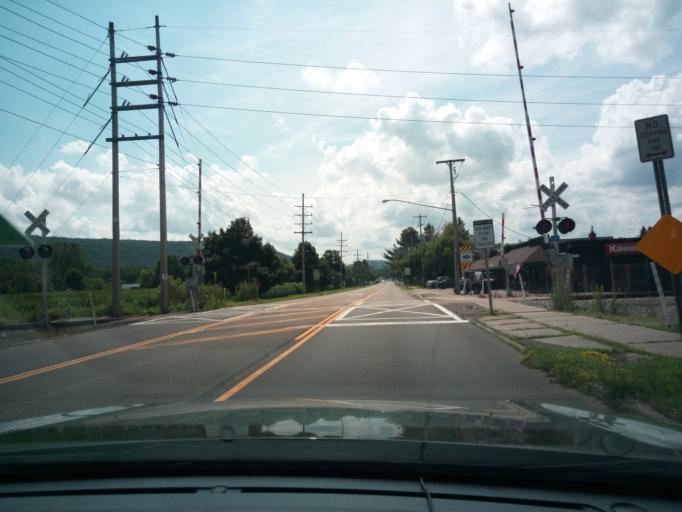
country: US
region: New York
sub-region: Chemung County
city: Southport
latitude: 42.0600
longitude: -76.7878
